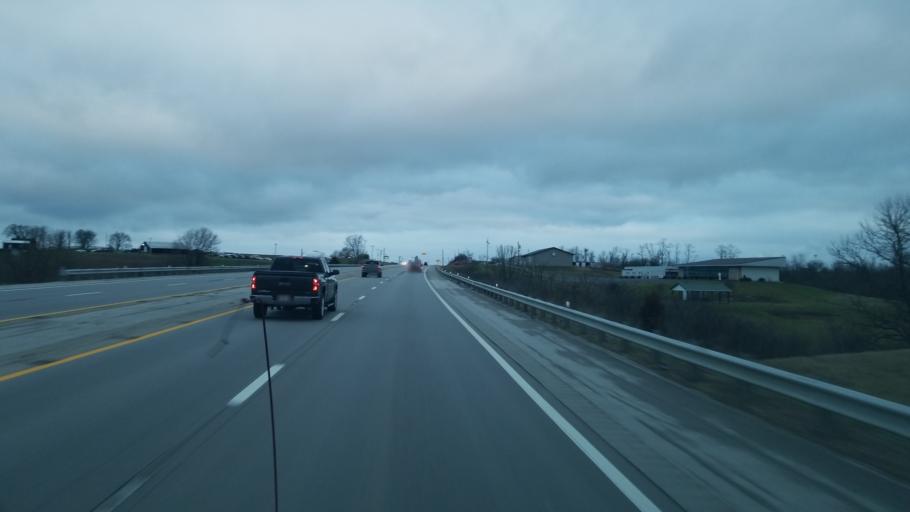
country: US
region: Kentucky
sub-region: Mason County
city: Maysville
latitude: 38.6128
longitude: -83.7745
